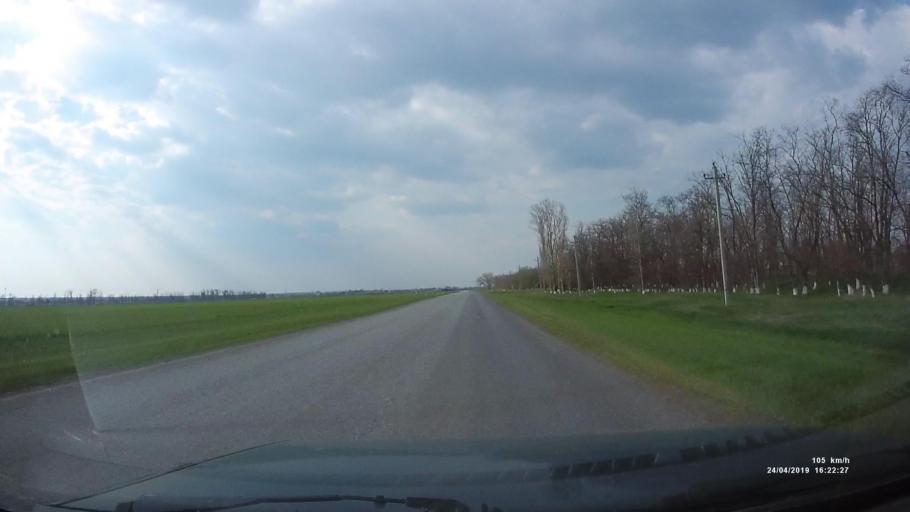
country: RU
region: Rostov
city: Orlovskiy
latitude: 46.8194
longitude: 42.0560
